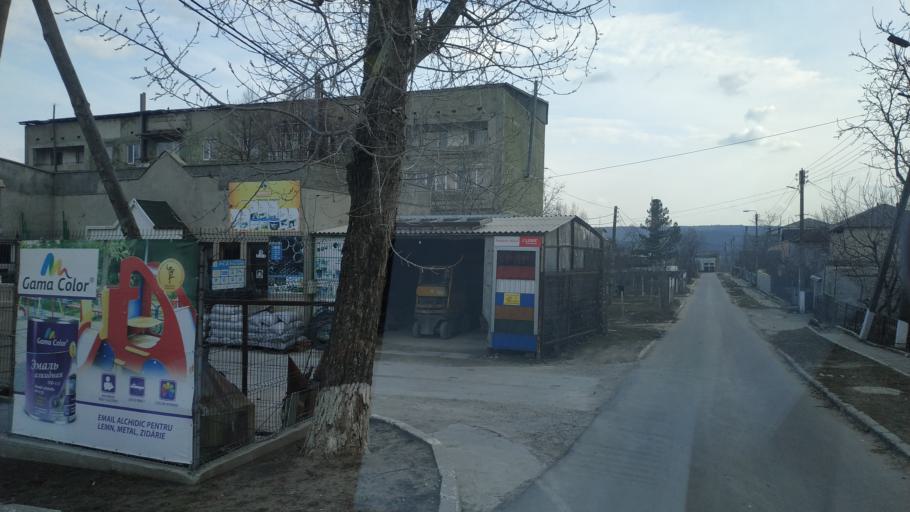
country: MD
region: Anenii Noi
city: Anenii Noi
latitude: 46.8991
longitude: 29.3099
